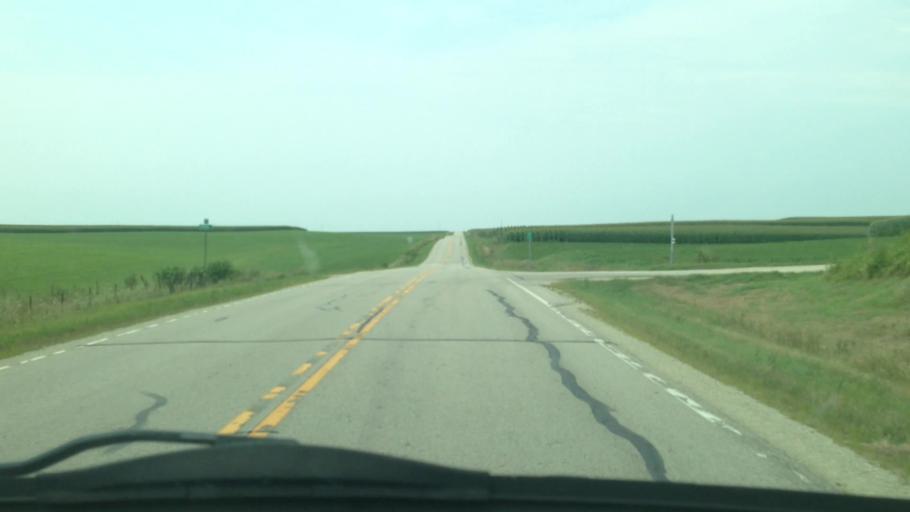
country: US
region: Minnesota
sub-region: Fillmore County
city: Preston
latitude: 43.7742
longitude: -91.9498
